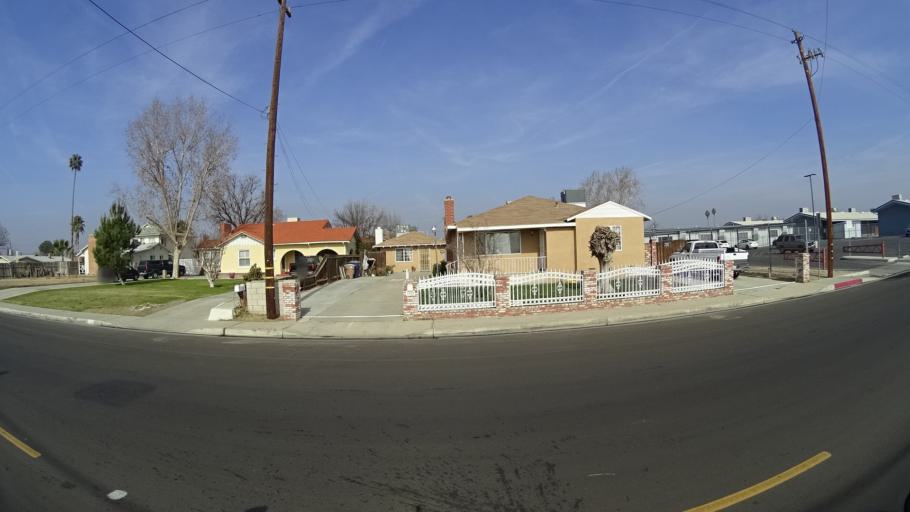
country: US
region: California
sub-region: Kern County
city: Bakersfield
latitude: 35.3466
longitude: -119.0142
